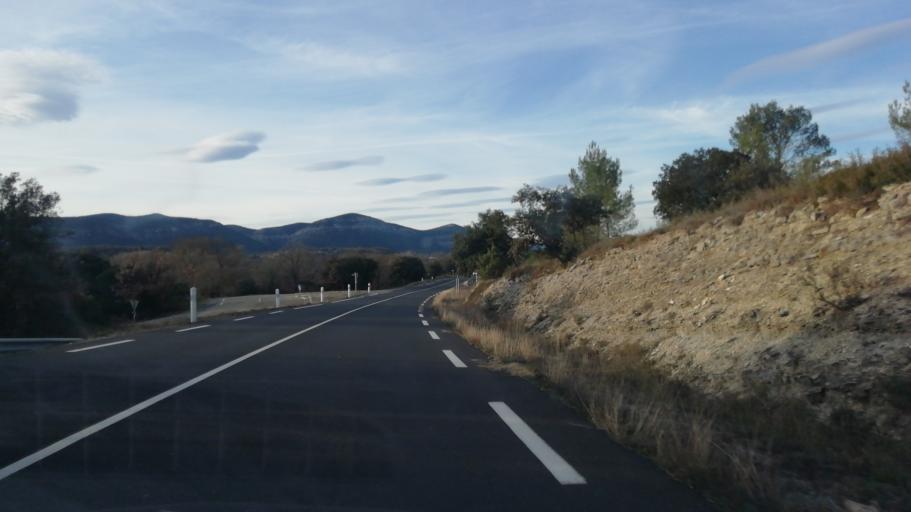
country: FR
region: Languedoc-Roussillon
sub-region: Departement du Gard
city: Quissac
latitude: 43.8863
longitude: 4.0175
